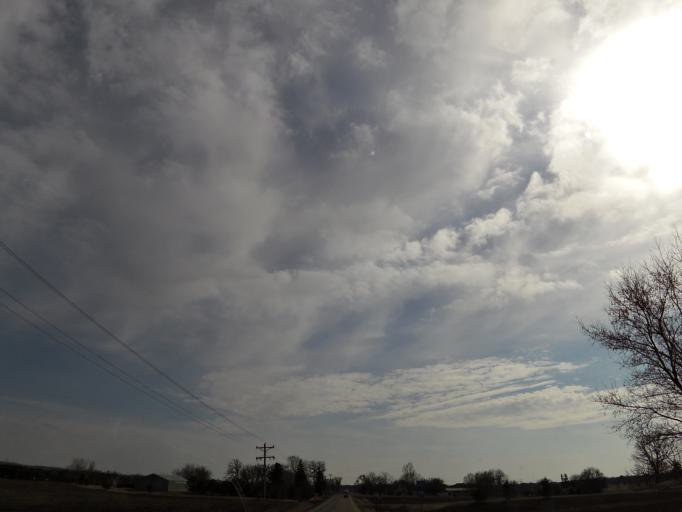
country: US
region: Minnesota
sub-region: Scott County
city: Prior Lake
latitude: 44.6772
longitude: -93.3792
